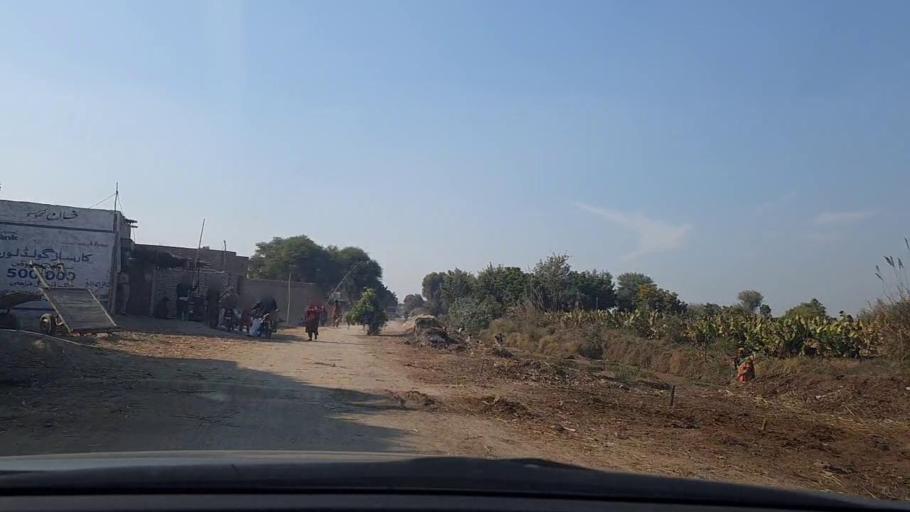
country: PK
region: Sindh
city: Daulatpur
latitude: 26.3052
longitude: 68.0884
